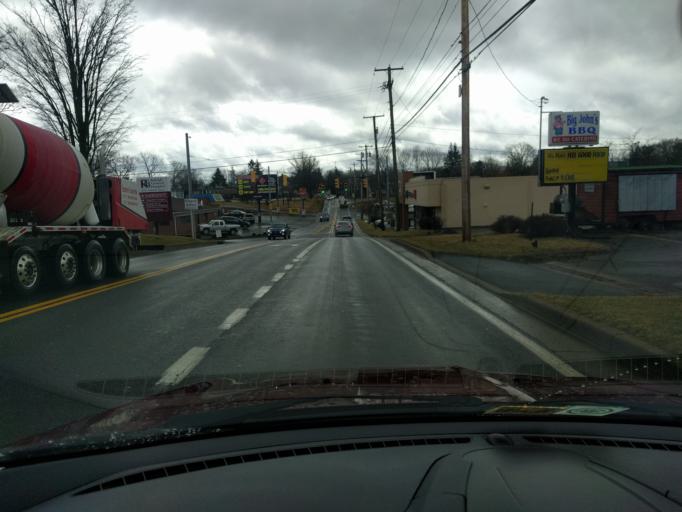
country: US
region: West Virginia
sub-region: Raleigh County
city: Mabscott
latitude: 37.7870
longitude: -81.2032
